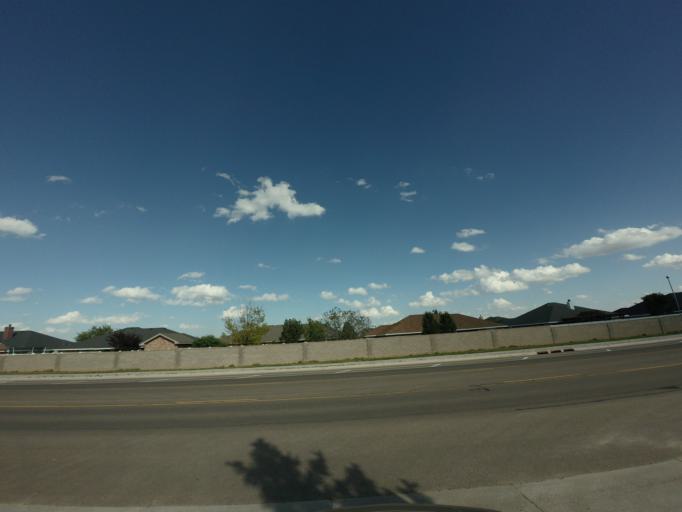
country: US
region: New Mexico
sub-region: Curry County
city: Clovis
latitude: 34.4378
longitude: -103.1787
